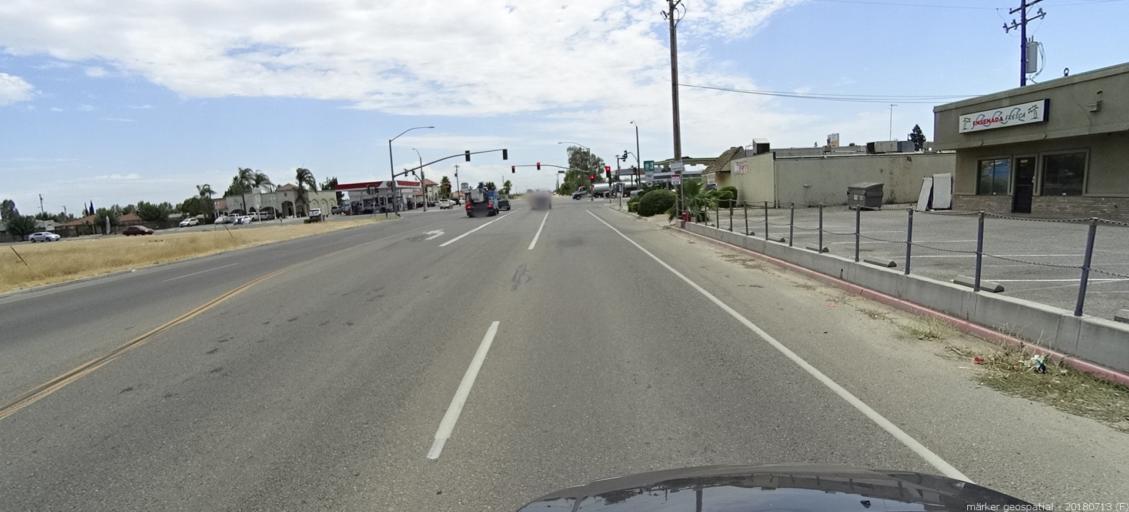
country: US
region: California
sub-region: Madera County
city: Madera Acres
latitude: 36.9963
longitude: -120.0752
